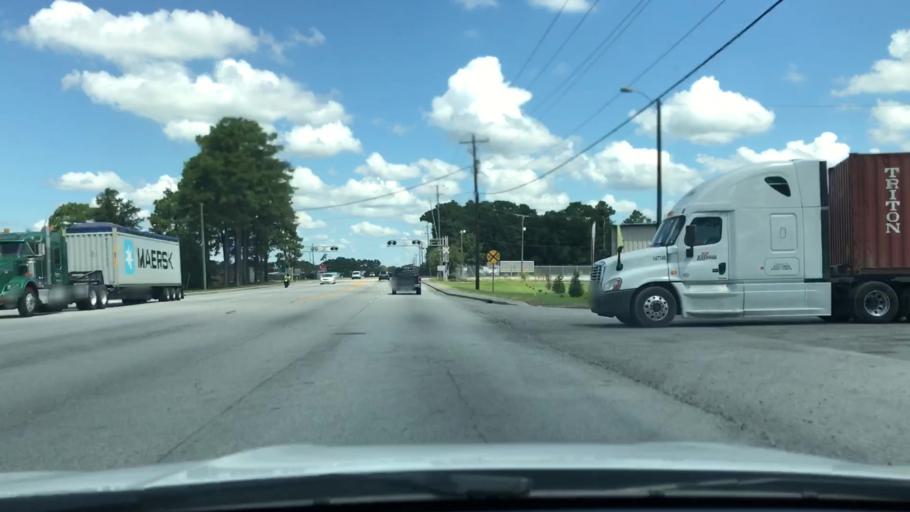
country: US
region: South Carolina
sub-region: Berkeley County
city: Hanahan
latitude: 32.9059
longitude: -79.9857
